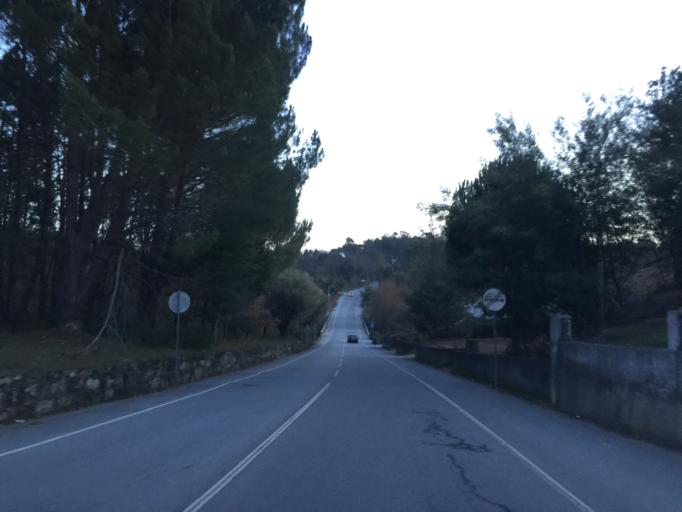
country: PT
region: Viseu
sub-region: Concelho de Carregal do Sal
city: Carregal do Sal
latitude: 40.4634
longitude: -7.9725
